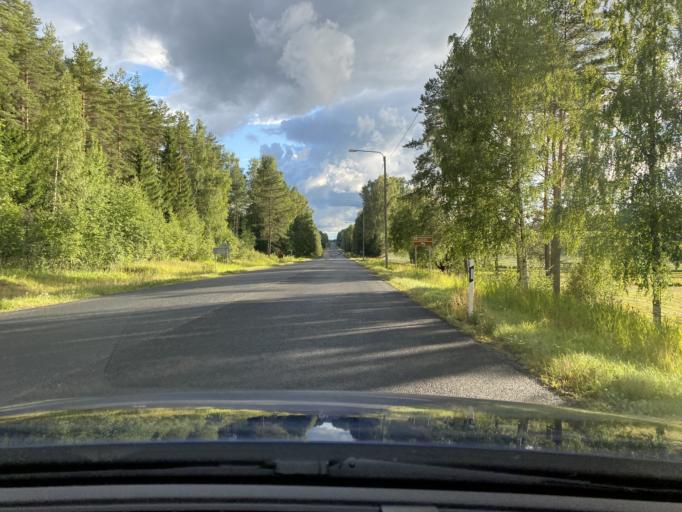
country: FI
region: Haeme
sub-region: Haemeenlinna
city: Renko
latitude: 60.9003
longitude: 24.2864
